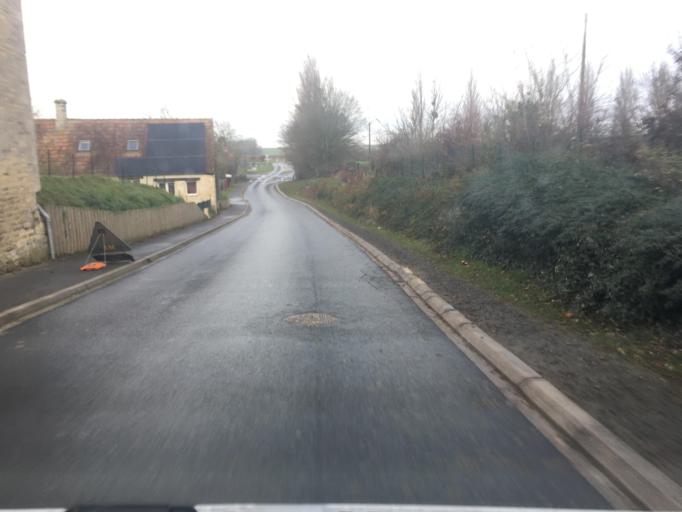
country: FR
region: Lower Normandy
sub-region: Departement du Calvados
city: Creully
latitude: 49.2525
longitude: -0.5625
